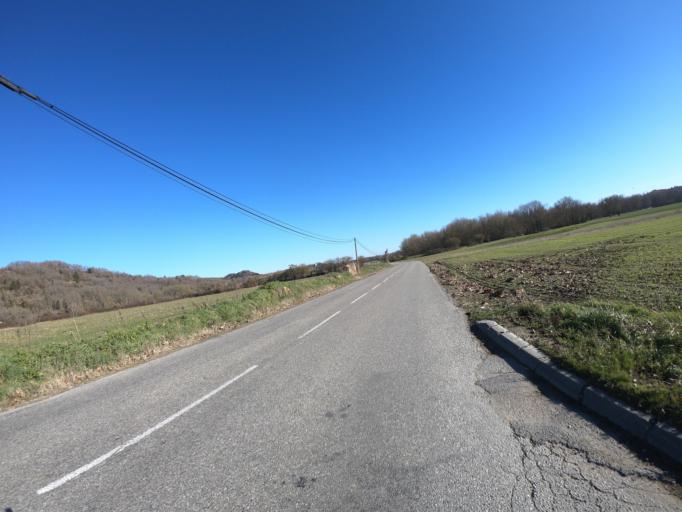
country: FR
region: Midi-Pyrenees
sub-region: Departement de l'Ariege
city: Mirepoix
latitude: 43.0947
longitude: 1.8469
